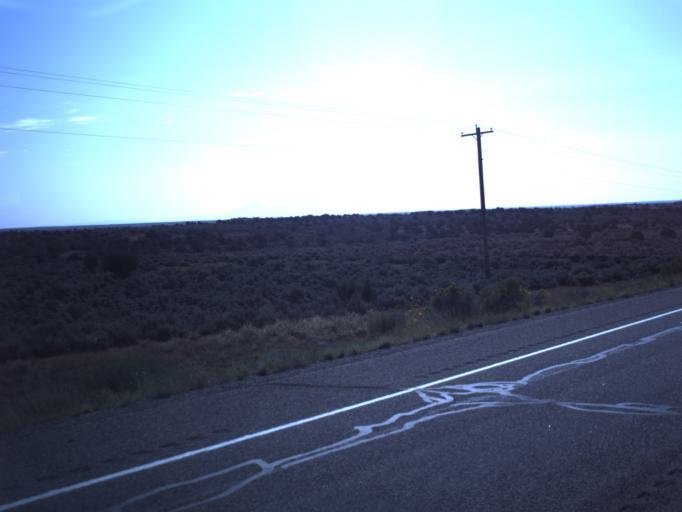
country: US
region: Utah
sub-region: San Juan County
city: Blanding
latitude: 37.4929
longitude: -109.4807
